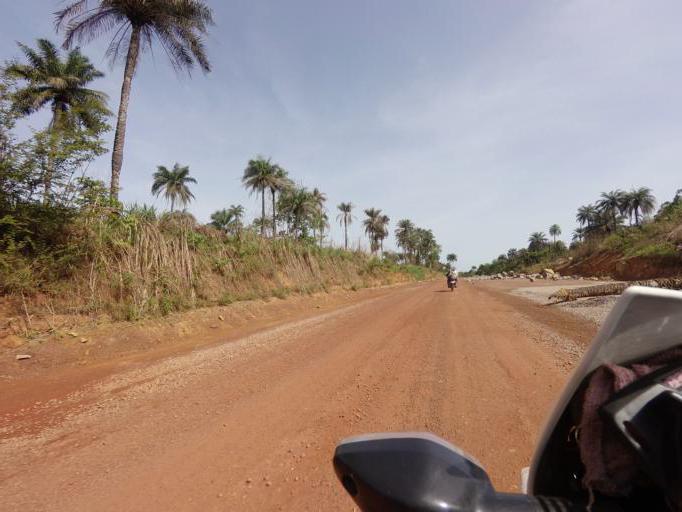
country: SL
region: Northern Province
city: Makeni
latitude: 9.0531
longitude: -12.1740
